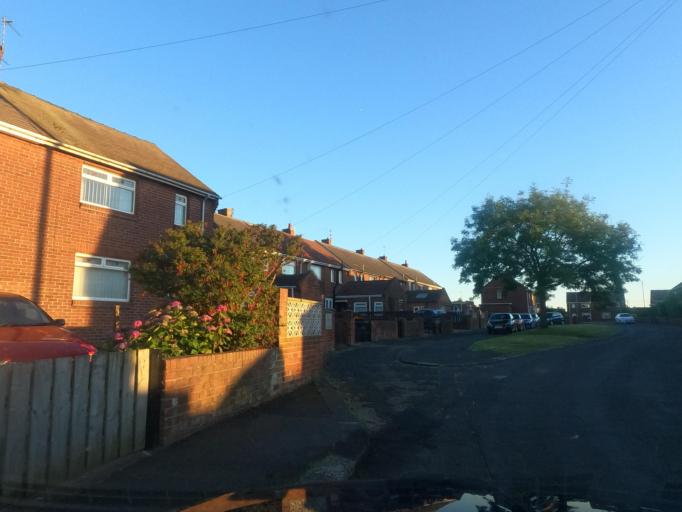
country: GB
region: England
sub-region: Northumberland
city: Newbiggin-by-the-Sea
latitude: 55.1789
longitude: -1.5212
